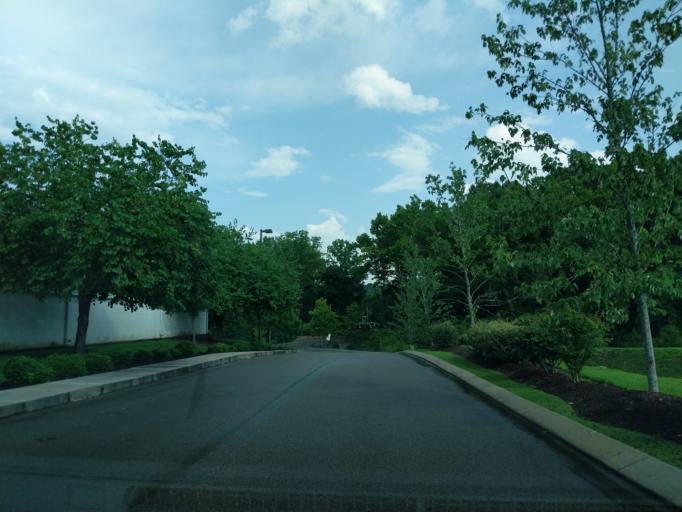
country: US
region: Tennessee
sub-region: Cheatham County
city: Pegram
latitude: 36.0429
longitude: -86.9587
